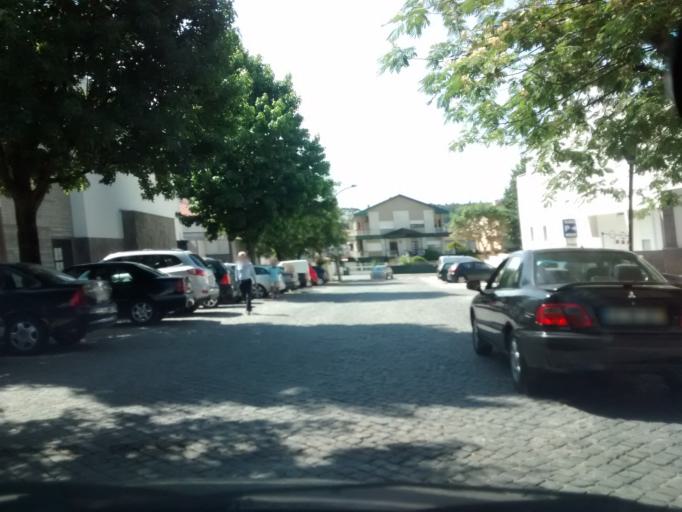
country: PT
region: Braga
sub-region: Braga
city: Braga
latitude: 41.5468
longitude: -8.4220
